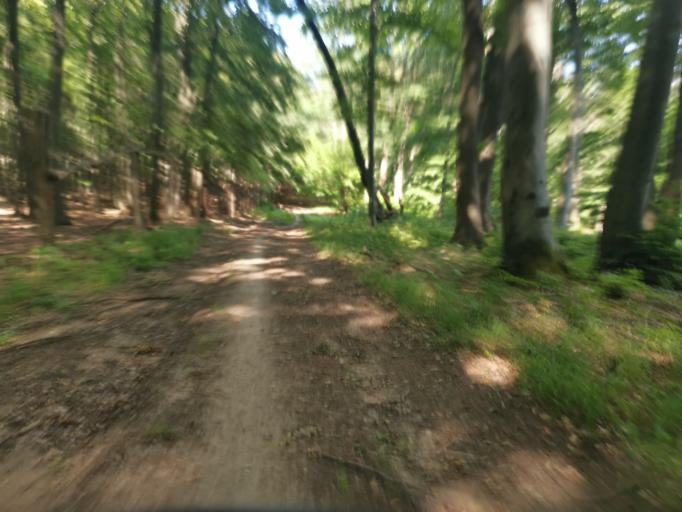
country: CZ
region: South Moravian
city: Knezdub
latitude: 48.8233
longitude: 17.4108
